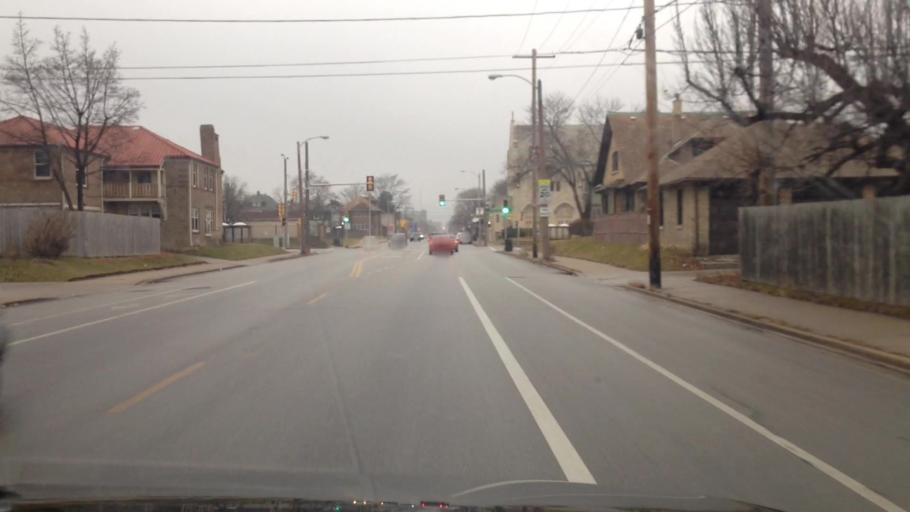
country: US
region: Wisconsin
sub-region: Milwaukee County
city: Wauwatosa
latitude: 43.0680
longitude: -87.9663
